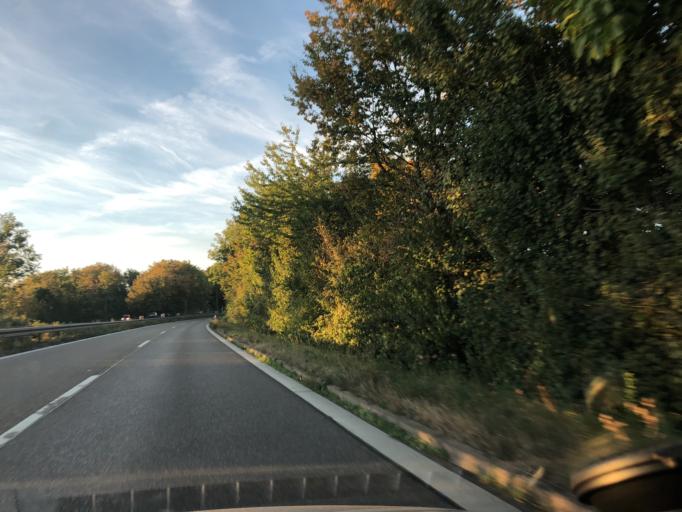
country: DE
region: Baden-Wuerttemberg
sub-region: Regierungsbezirk Stuttgart
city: Ludwigsburg
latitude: 48.8805
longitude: 9.1956
